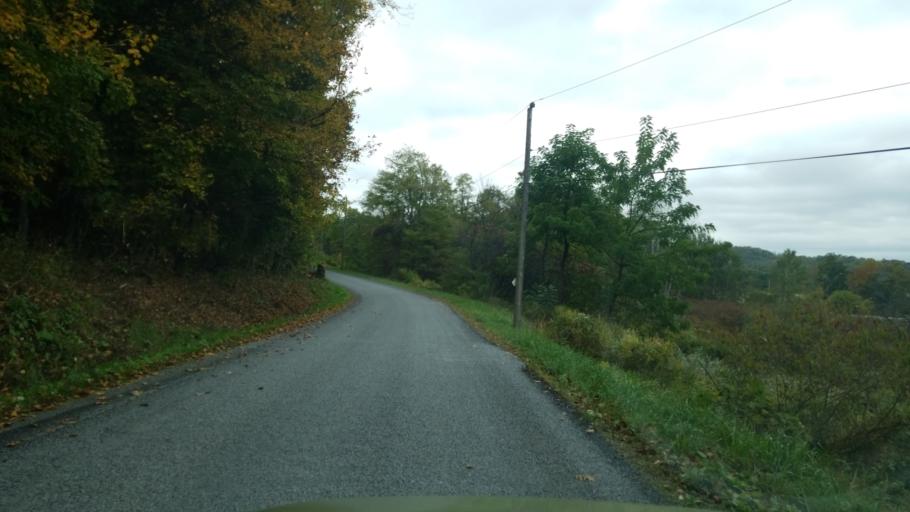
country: US
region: Pennsylvania
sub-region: Clearfield County
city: Curwensville
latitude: 40.9663
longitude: -78.4982
